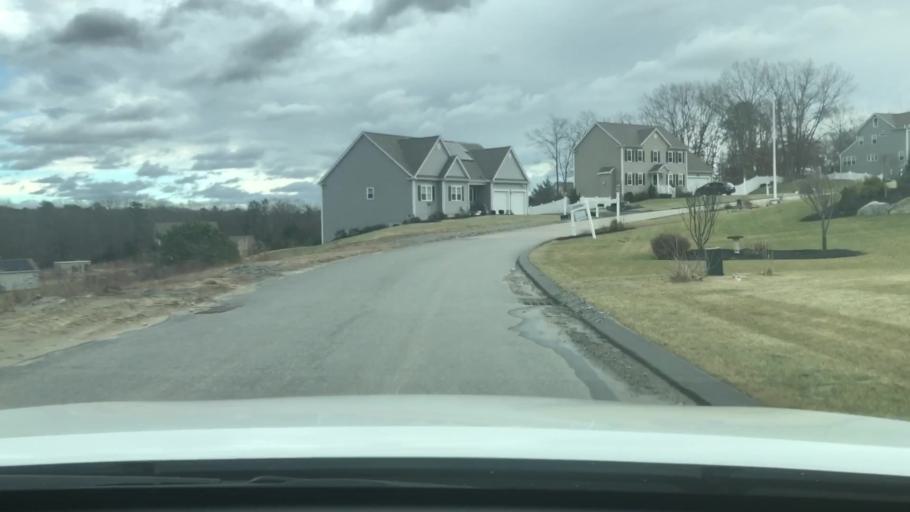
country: US
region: Rhode Island
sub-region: Providence County
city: Woonsocket
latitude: 42.0356
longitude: -71.5113
